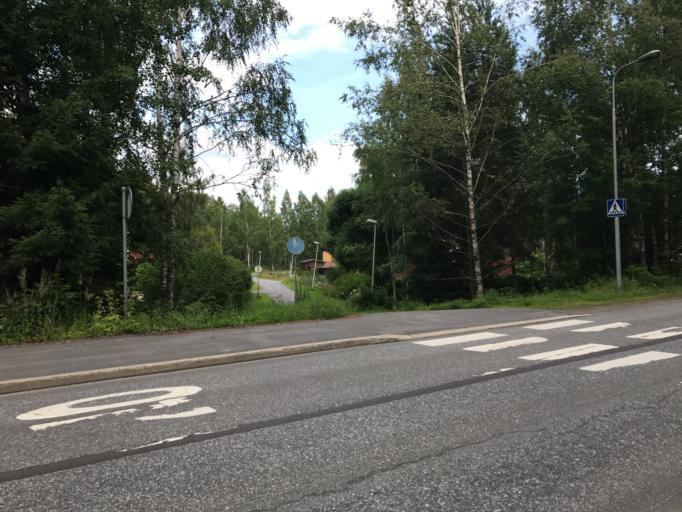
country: FI
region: Pirkanmaa
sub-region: Etelae-Pirkanmaa
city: Valkeakoski
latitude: 61.2521
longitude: 24.0482
